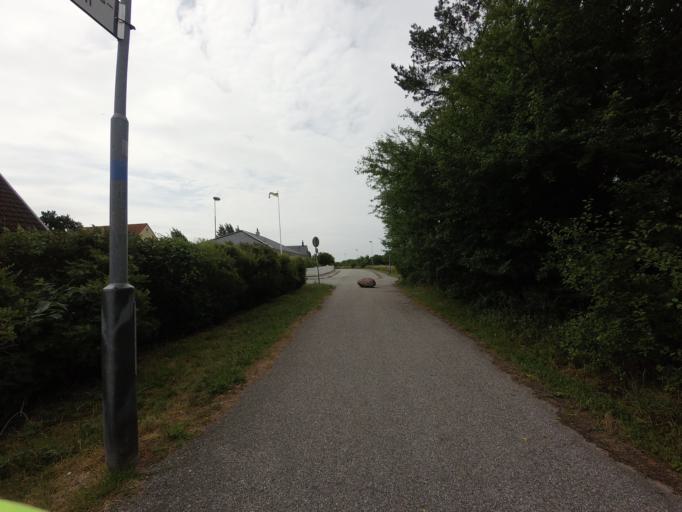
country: SE
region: Skane
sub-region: Malmo
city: Bunkeflostrand
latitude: 55.5597
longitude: 12.9080
